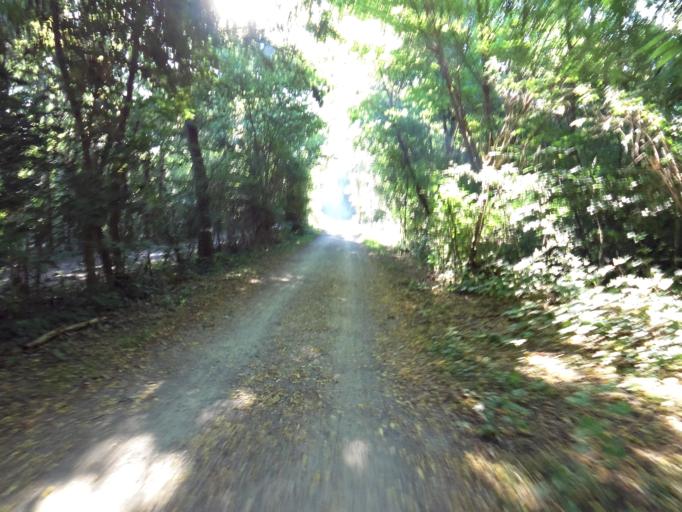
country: DE
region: Rheinland-Pfalz
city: Gartenstadt
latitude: 49.4561
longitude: 8.3896
